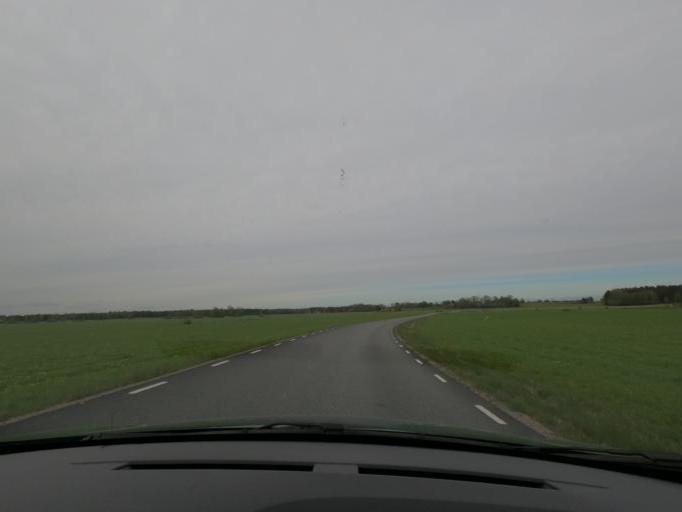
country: SE
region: Joenkoeping
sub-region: Varnamo Kommun
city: Bredaryd
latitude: 57.1278
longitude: 13.6832
